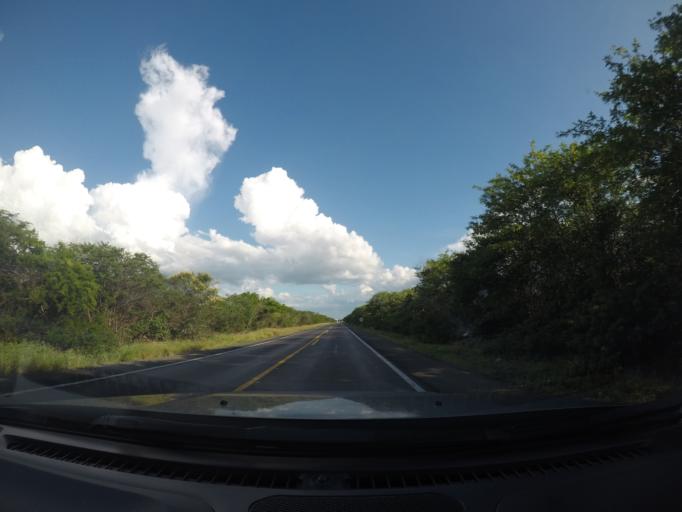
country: BR
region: Bahia
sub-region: Oliveira Dos Brejinhos
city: Oliveira dos Brejinhos
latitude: -12.0932
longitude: -42.9272
